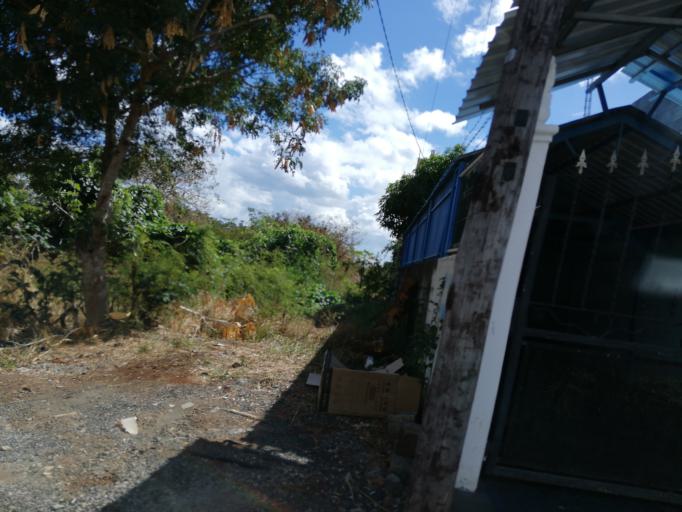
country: MU
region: Black River
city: Petite Riviere
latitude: -20.1942
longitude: 57.4641
